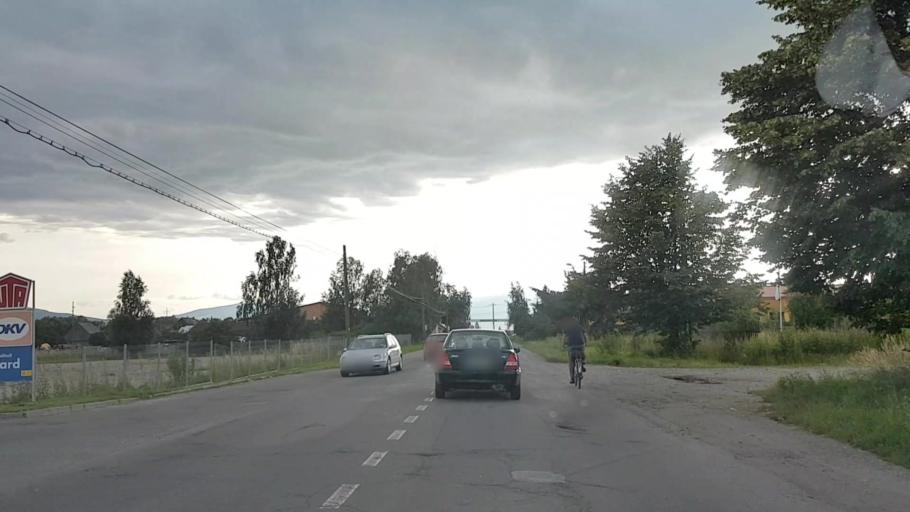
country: RO
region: Harghita
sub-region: Municipiul Gheorgheni
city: Gheorgheni
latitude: 46.7132
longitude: 25.5668
